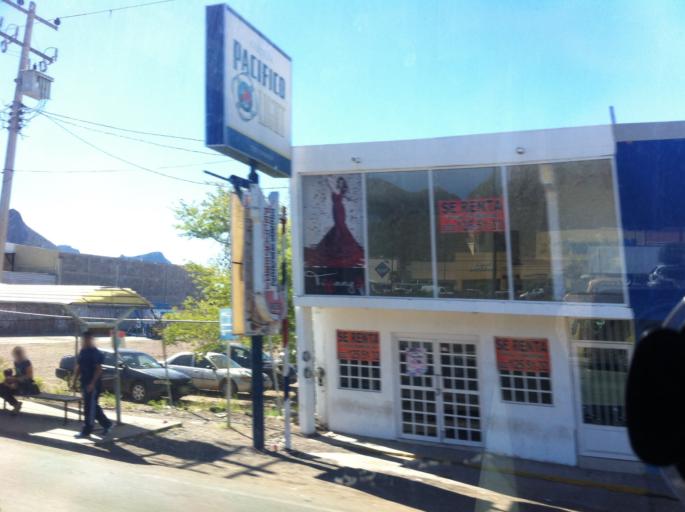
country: MX
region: Sonora
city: Heroica Guaymas
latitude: 27.9358
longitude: -110.9286
